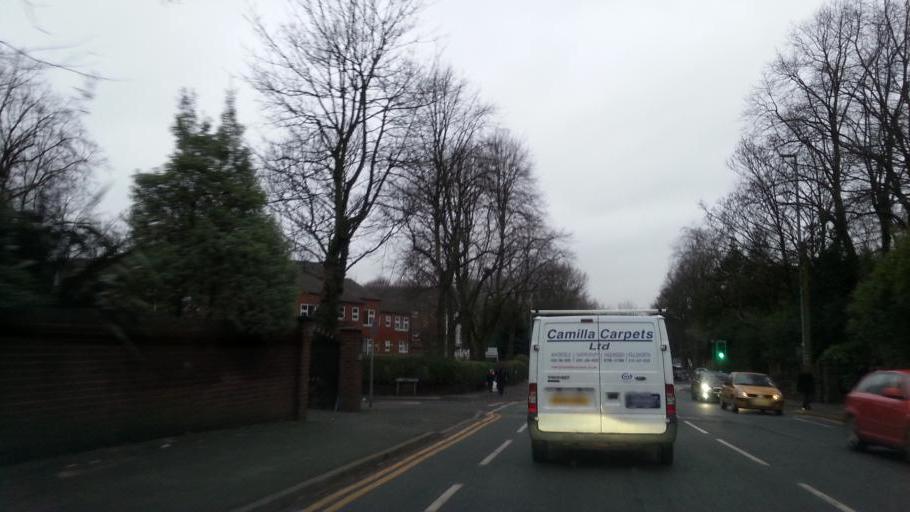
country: GB
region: England
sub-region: Borough of Bury
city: Prestwich
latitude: 53.5157
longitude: -2.2699
